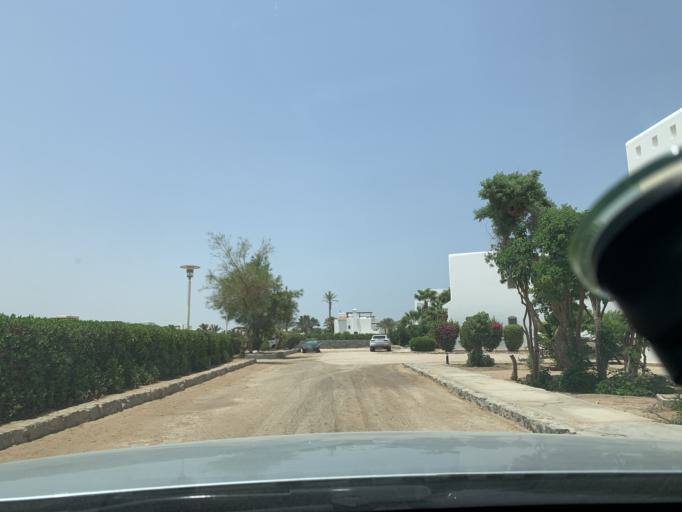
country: EG
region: Red Sea
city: El Gouna
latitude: 27.3689
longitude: 33.6712
